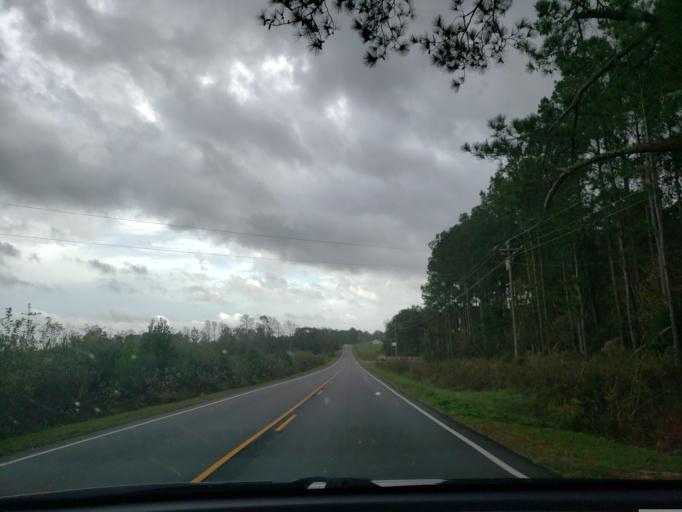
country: US
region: North Carolina
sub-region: Duplin County
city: Beulaville
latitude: 34.8612
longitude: -77.8789
